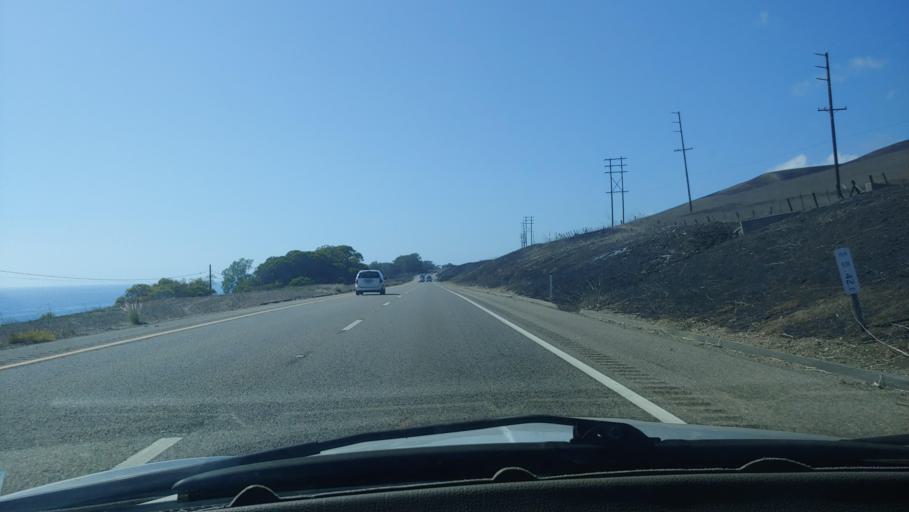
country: US
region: California
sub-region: Santa Barbara County
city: Solvang
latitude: 34.4736
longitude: -120.1576
